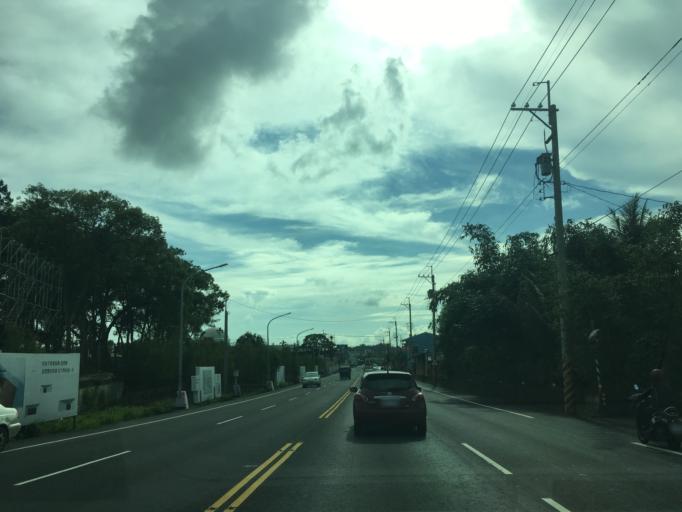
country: TW
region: Taiwan
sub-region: Chiayi
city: Jiayi Shi
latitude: 23.4422
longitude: 120.5193
